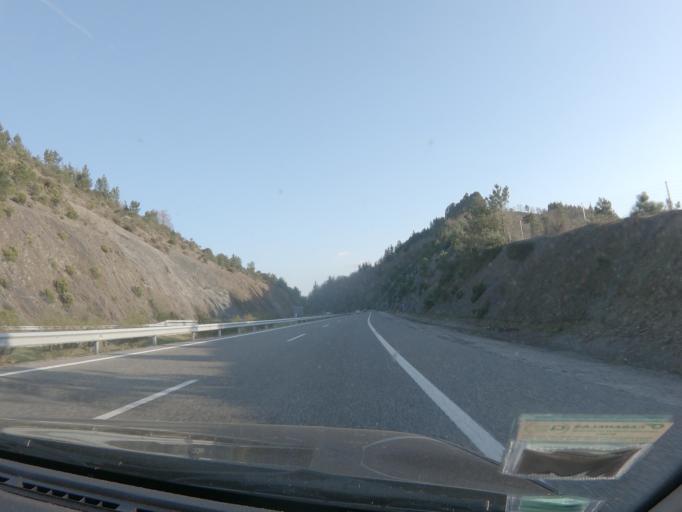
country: ES
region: Galicia
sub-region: Provincia de Lugo
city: Becerrea
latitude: 42.8554
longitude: -7.1272
